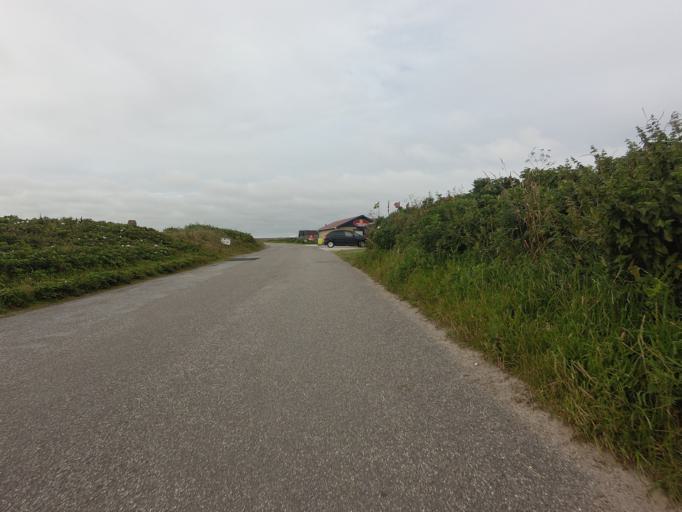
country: DK
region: North Denmark
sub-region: Jammerbugt Kommune
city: Pandrup
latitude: 57.3858
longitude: 9.7254
